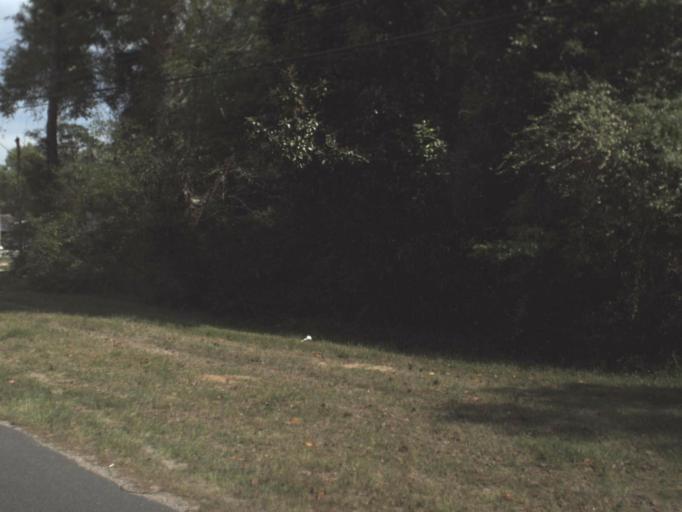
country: US
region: Florida
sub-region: Santa Rosa County
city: Bagdad
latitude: 30.6024
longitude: -87.0790
